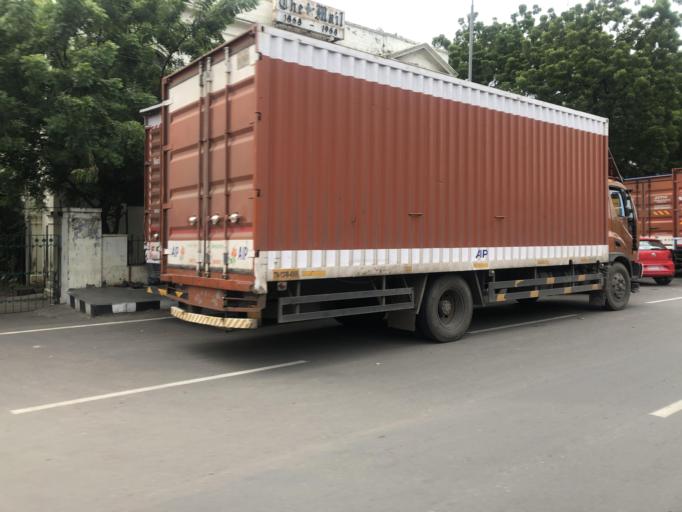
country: IN
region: Tamil Nadu
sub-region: Chennai
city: Chennai
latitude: 13.0701
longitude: 80.2732
